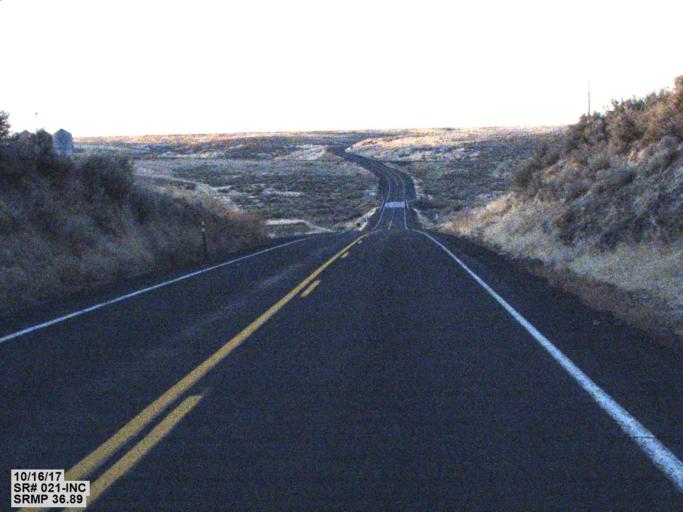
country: US
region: Washington
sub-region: Adams County
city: Ritzville
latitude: 47.0844
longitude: -118.6645
